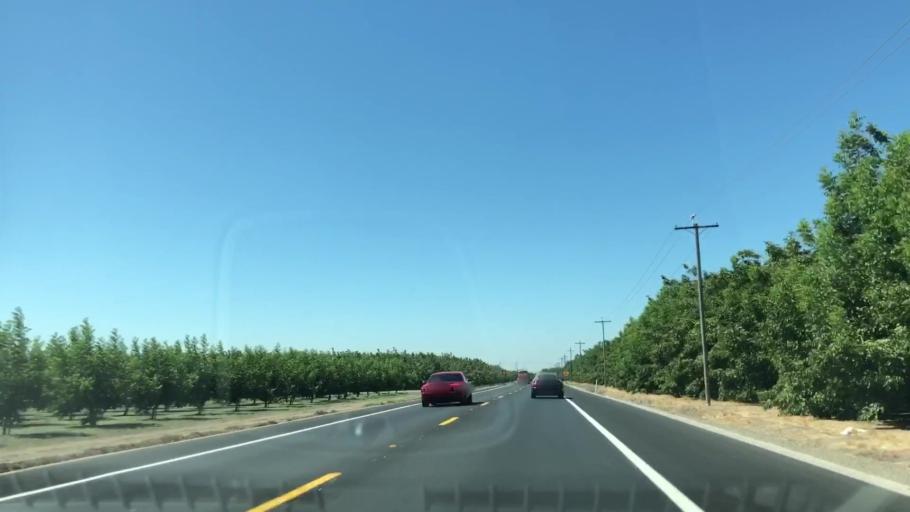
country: US
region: California
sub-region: San Joaquin County
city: Garden Acres
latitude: 37.9422
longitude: -121.1421
